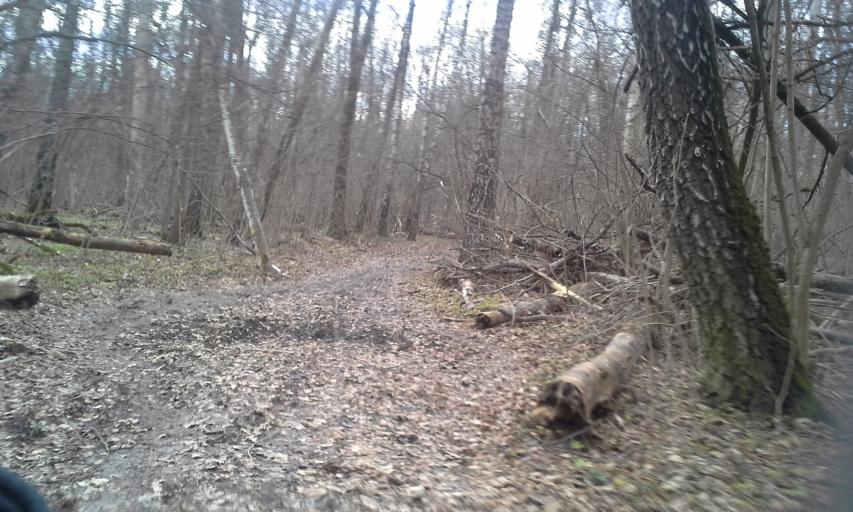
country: RU
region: Moscow
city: Yasenevo
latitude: 55.5668
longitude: 37.5372
